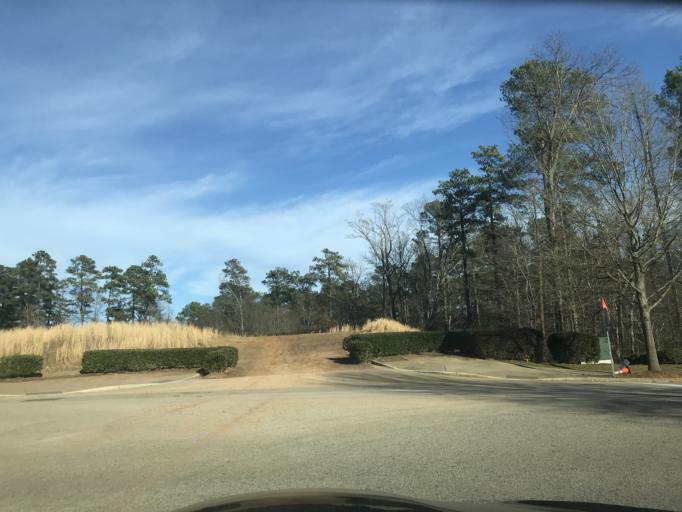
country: US
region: North Carolina
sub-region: Wake County
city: Cary
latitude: 35.8057
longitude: -78.7279
